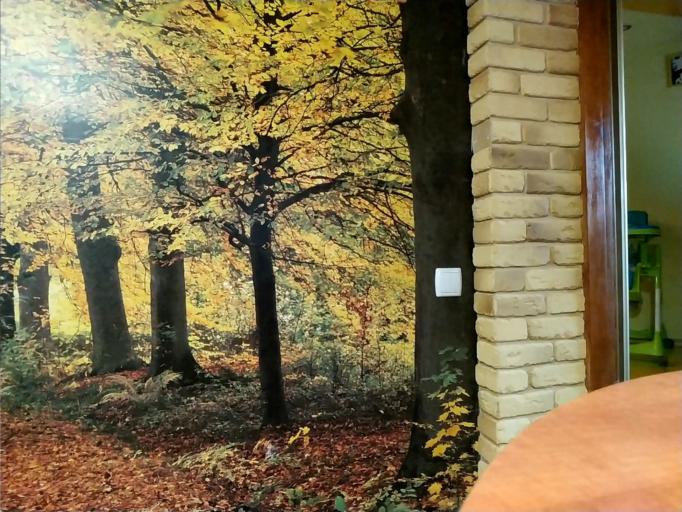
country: BY
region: Minsk
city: Il'ya
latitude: 54.4220
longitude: 27.4622
